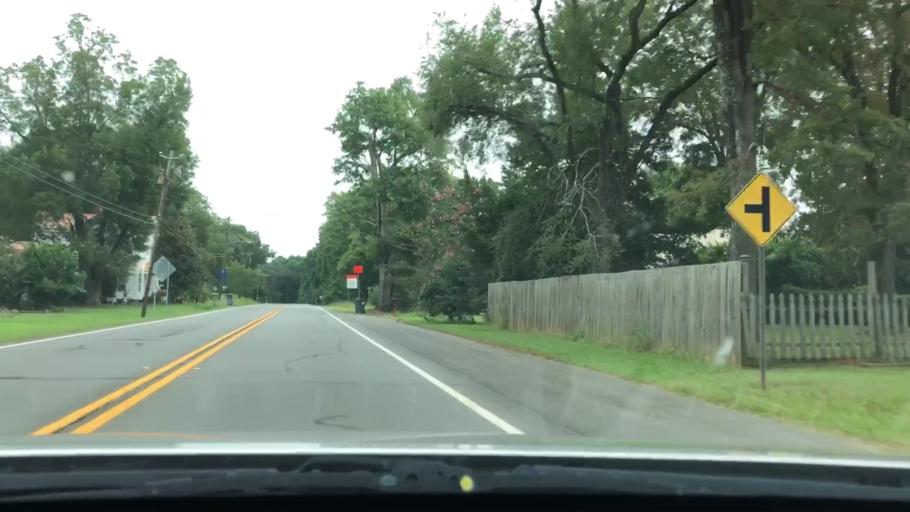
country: US
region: Georgia
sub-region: Upson County
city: Hannahs Mill
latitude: 33.0138
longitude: -84.4993
